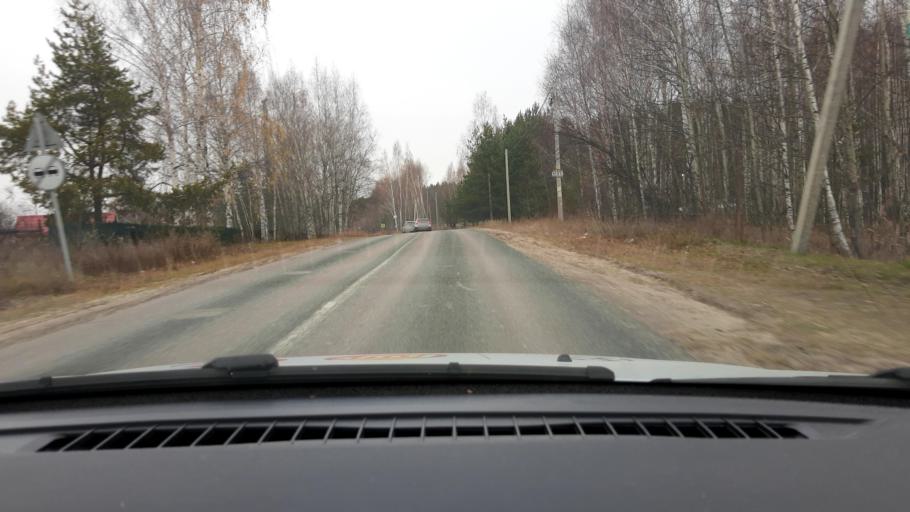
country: RU
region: Nizjnij Novgorod
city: Neklyudovo
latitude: 56.4404
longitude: 43.9105
